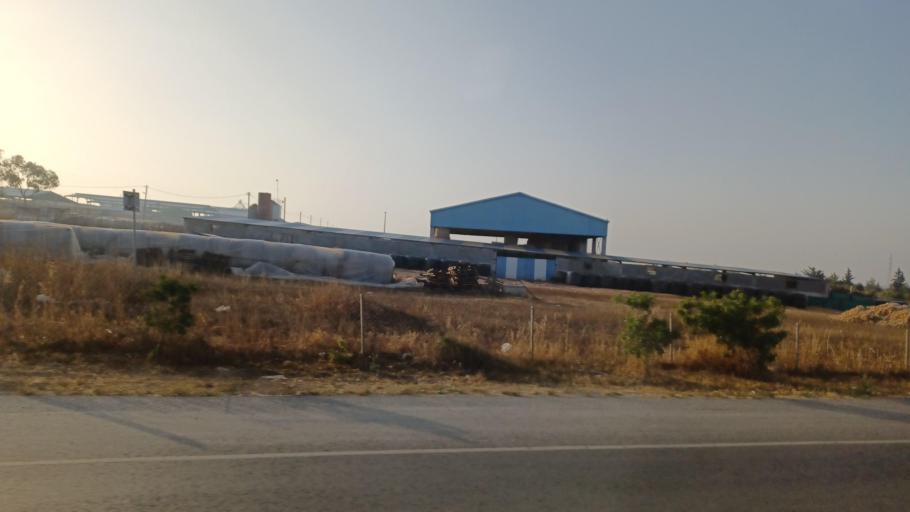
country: CY
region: Ammochostos
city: Frenaros
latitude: 35.0085
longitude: 33.9385
